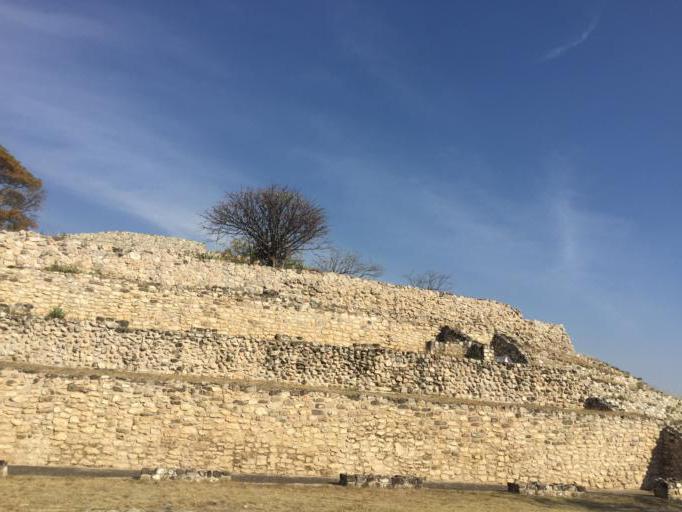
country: MX
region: Morelos
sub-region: Miacatlan
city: Xochicalco (Cirenio Longares)
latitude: 18.8034
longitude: -99.2969
